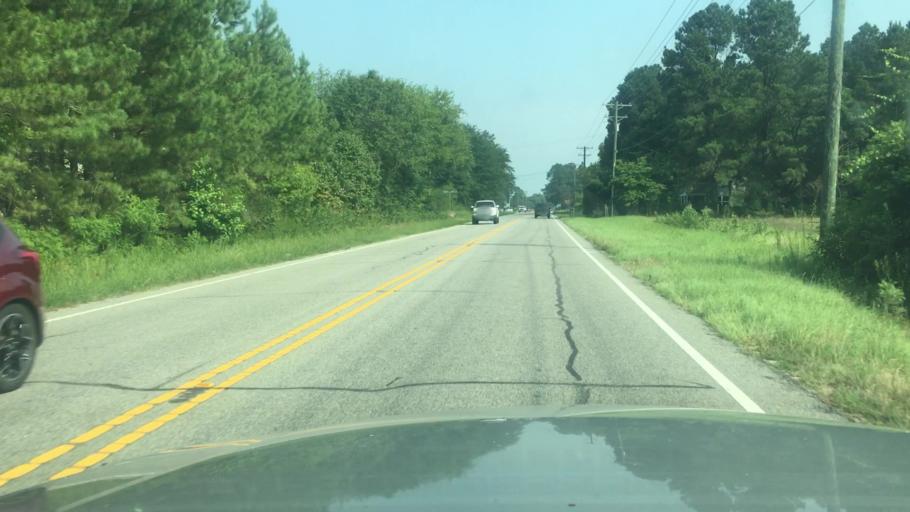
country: US
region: North Carolina
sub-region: Cumberland County
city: Hope Mills
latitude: 34.9128
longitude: -78.9061
